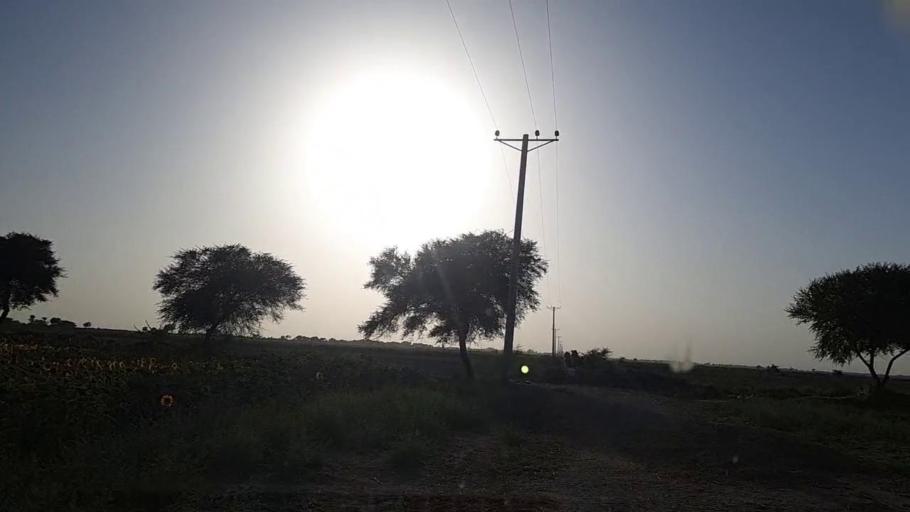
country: PK
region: Sindh
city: Jati
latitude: 24.4224
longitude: 68.2850
